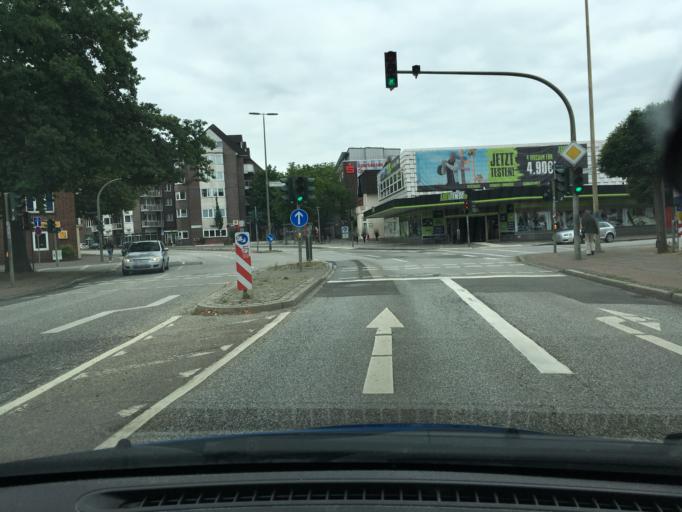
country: DE
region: Schleswig-Holstein
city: Geesthacht
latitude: 53.4379
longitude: 10.3678
